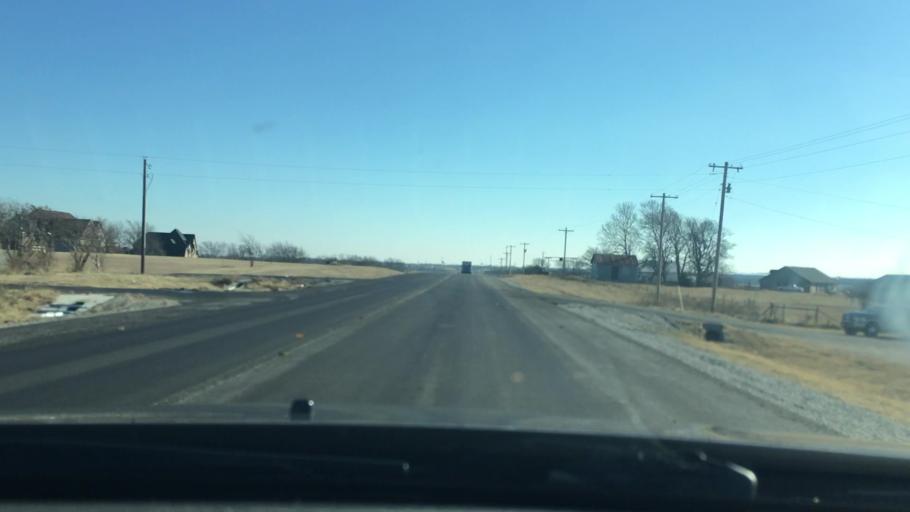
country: US
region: Oklahoma
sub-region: Love County
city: Marietta
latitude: 33.9404
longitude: -97.1570
